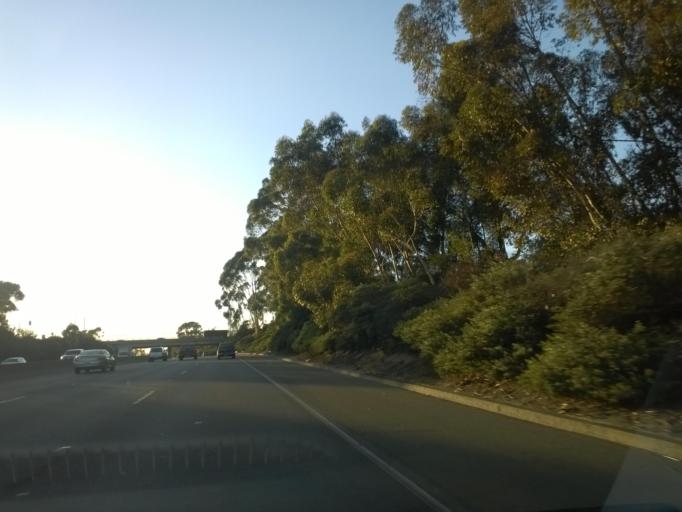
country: US
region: California
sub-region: Santa Barbara County
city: Mission Canyon
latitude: 34.4277
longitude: -119.7316
